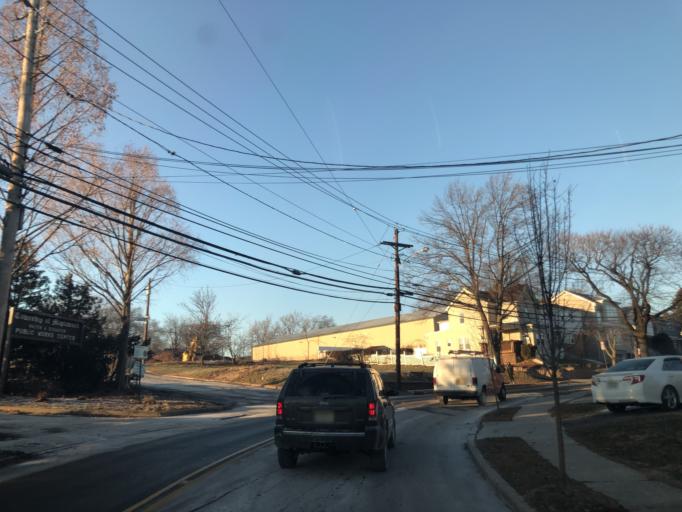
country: US
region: New Jersey
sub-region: Essex County
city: Maplewood
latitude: 40.7193
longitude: -74.2569
